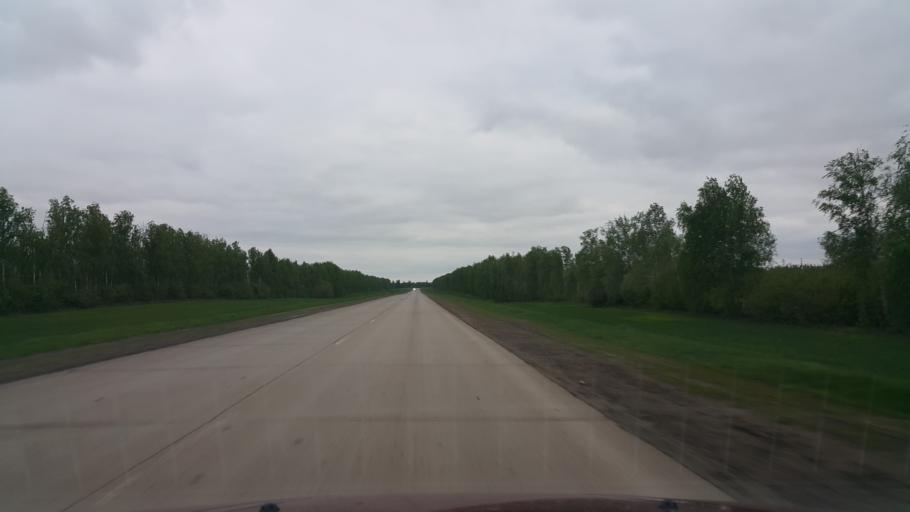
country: RU
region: Tambov
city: Znamenka
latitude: 52.3878
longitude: 41.4315
